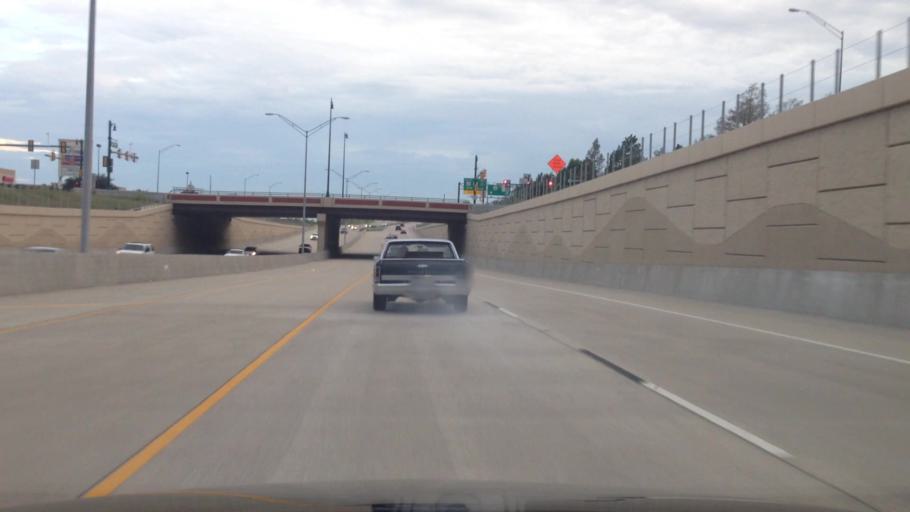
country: US
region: Texas
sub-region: Dallas County
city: Coppell
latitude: 32.9713
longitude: -97.0369
